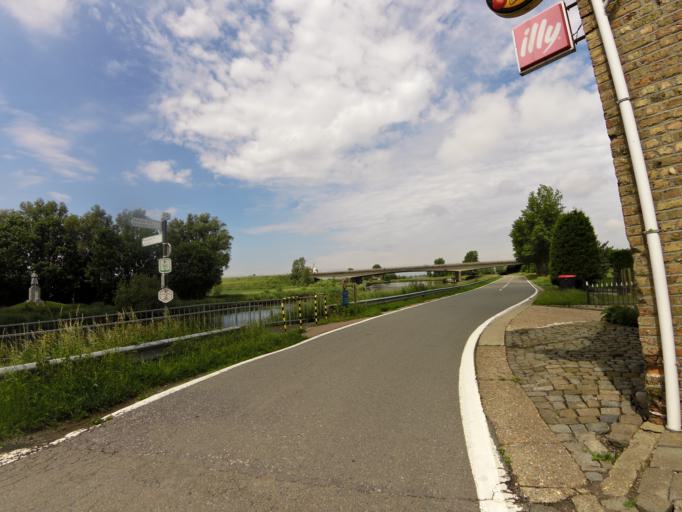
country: BE
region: Flanders
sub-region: Provincie West-Vlaanderen
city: Nieuwpoort
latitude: 51.1272
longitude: 2.8022
